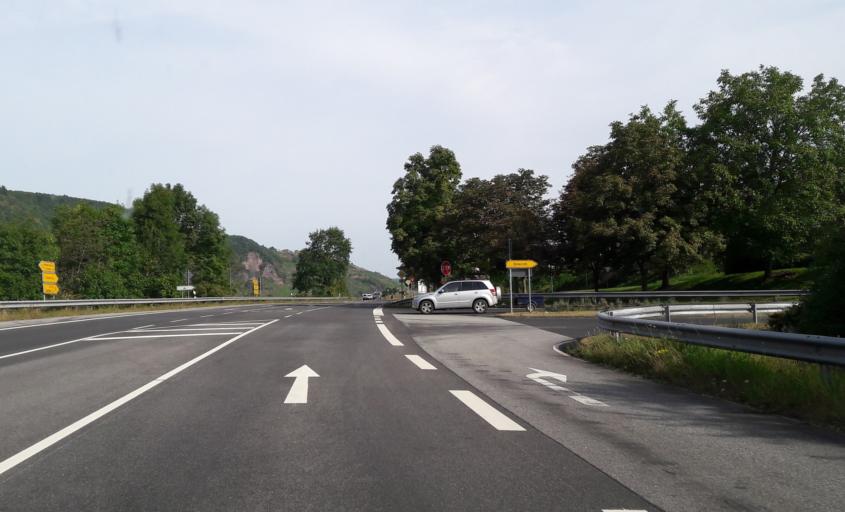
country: DE
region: Rheinland-Pfalz
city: Enkirch
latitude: 49.9890
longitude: 7.1186
